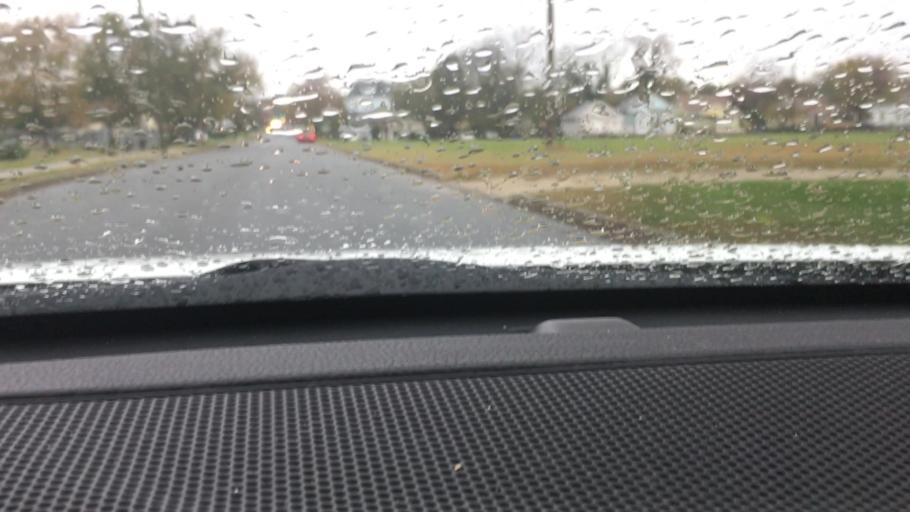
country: US
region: New Jersey
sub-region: Atlantic County
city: Northfield
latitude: 39.3802
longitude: -74.5374
